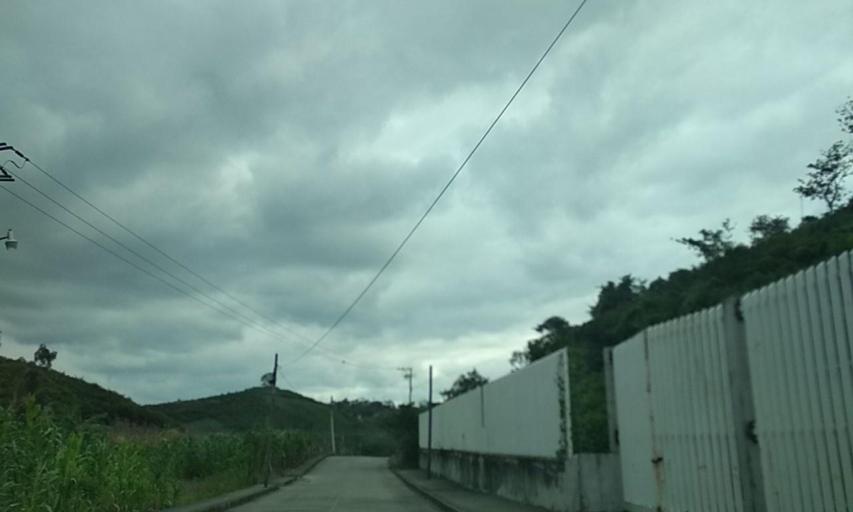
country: MX
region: Veracruz
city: Papantla de Olarte
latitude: 20.4726
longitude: -97.3204
